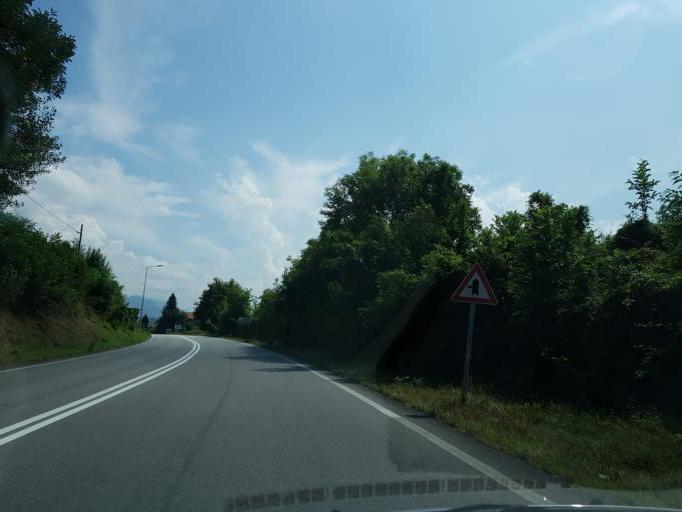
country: IT
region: Piedmont
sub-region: Provincia di Cuneo
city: Borgo San Dalmazzo
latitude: 44.3403
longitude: 7.4763
